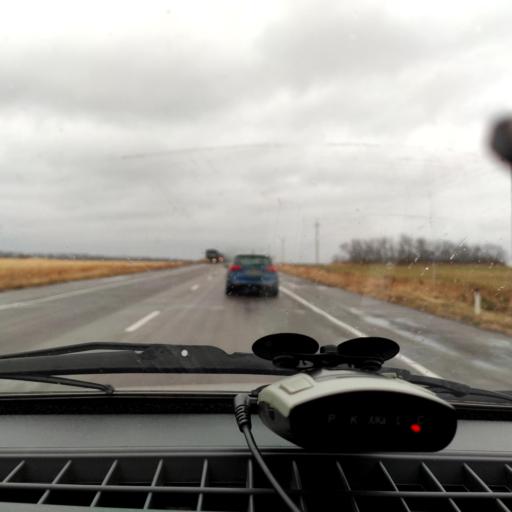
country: RU
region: Voronezj
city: Strelitsa
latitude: 51.5599
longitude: 38.9732
